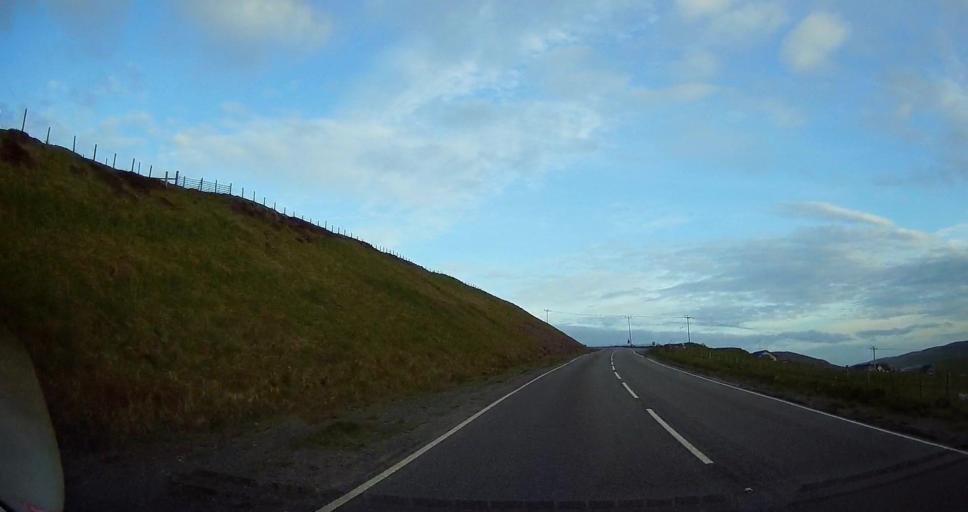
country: GB
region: Scotland
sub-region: Shetland Islands
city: Lerwick
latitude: 60.1839
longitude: -1.2242
